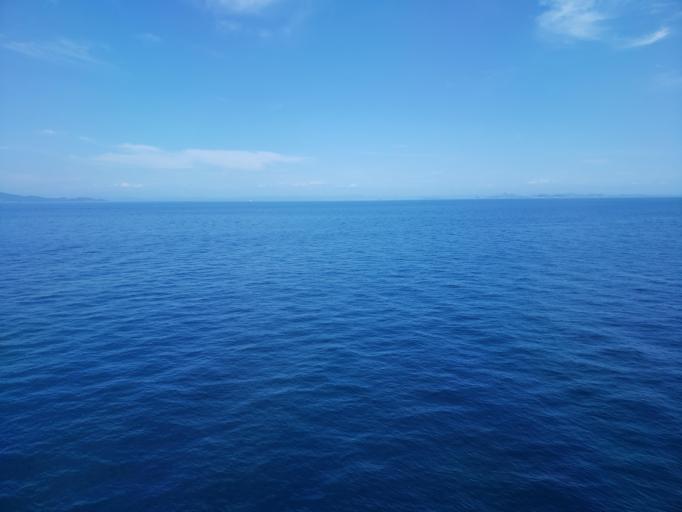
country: JP
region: Tokushima
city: Narutocho-mitsuishi
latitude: 34.4640
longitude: 134.4758
